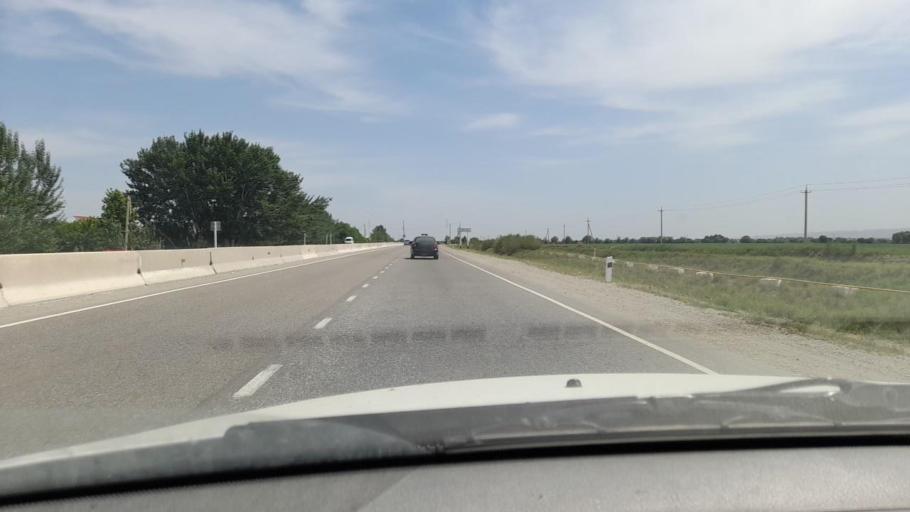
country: UZ
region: Navoiy
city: Karmana Shahri
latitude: 40.1272
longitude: 65.4598
